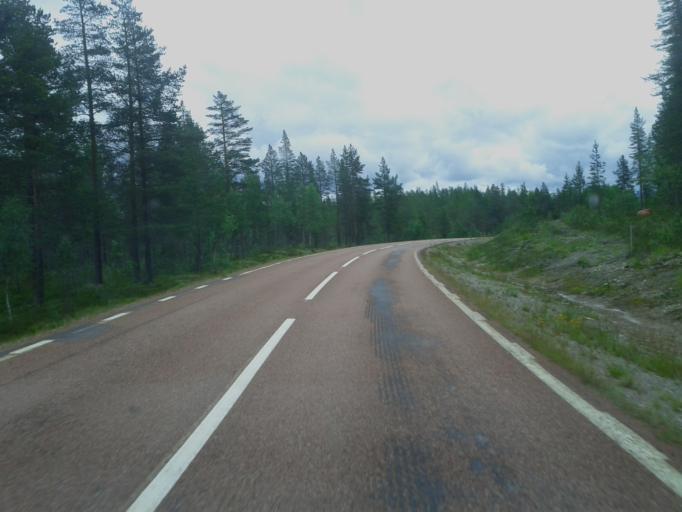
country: NO
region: Hedmark
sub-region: Engerdal
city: Engerdal
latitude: 61.8053
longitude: 12.3931
